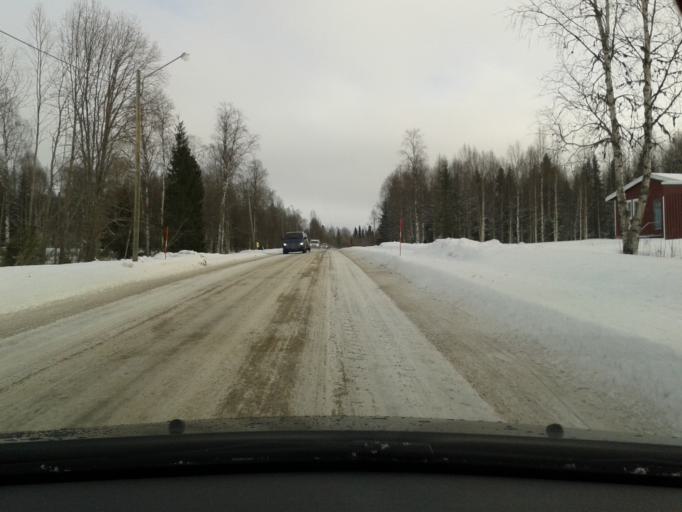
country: SE
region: Vaesterbotten
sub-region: Vilhelmina Kommun
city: Sjoberg
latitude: 64.7932
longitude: 16.0829
